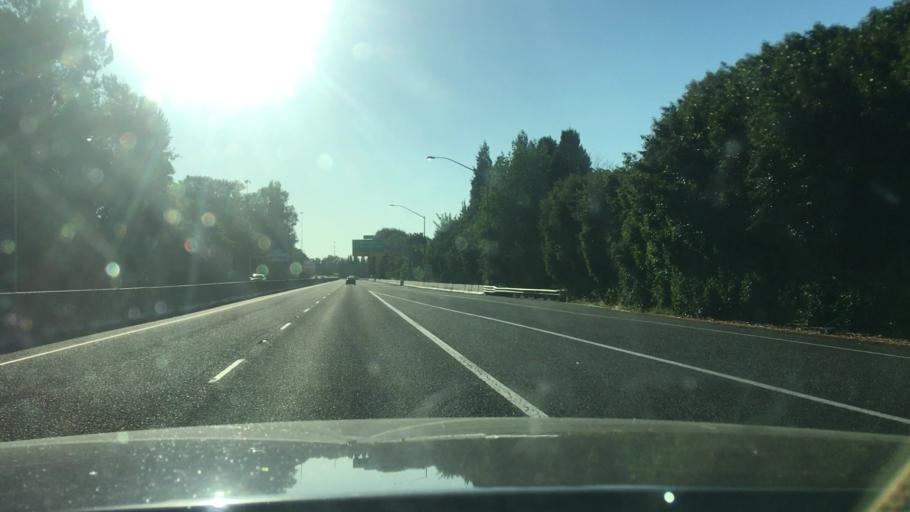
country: US
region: Oregon
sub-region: Lane County
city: Eugene
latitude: 44.0616
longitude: -123.0886
